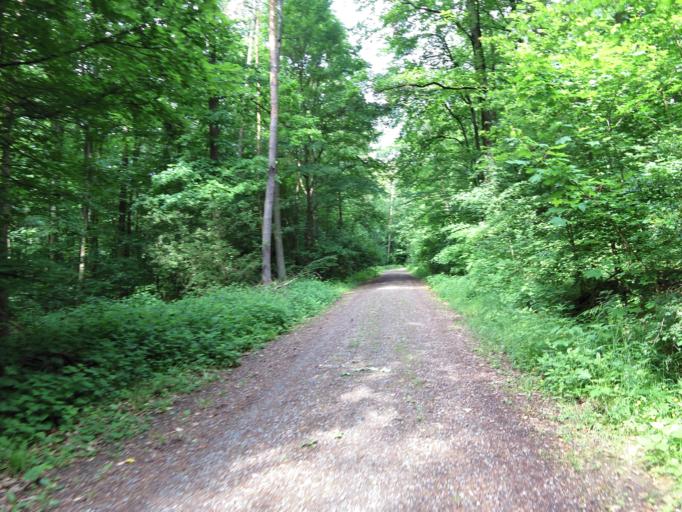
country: DE
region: Bavaria
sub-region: Regierungsbezirk Unterfranken
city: Kist
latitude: 49.7290
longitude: 9.8498
